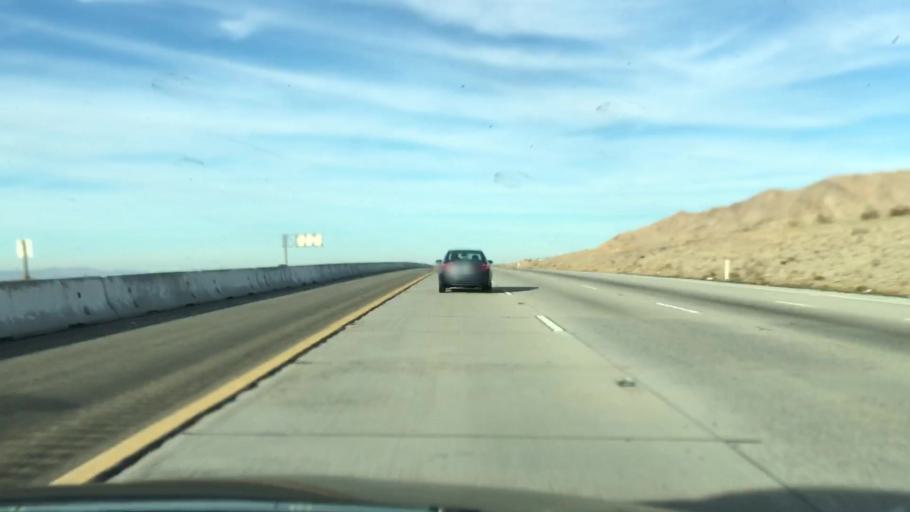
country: US
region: California
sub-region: San Bernardino County
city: Victorville
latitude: 34.7050
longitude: -117.2034
